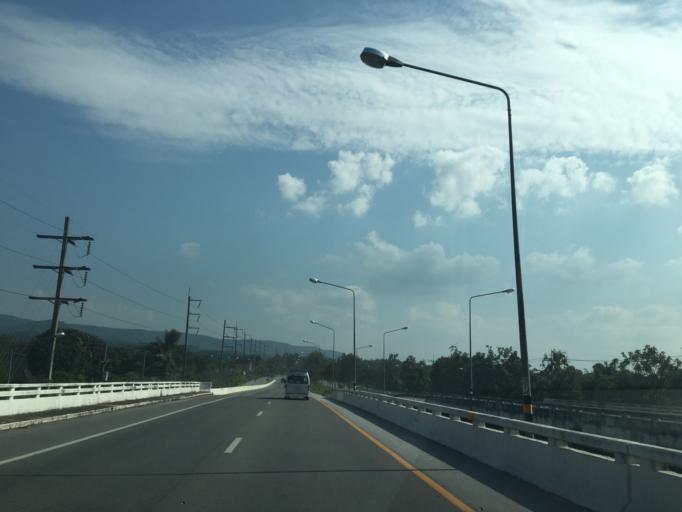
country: TH
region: Chiang Rai
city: Mae Lao
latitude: 19.7145
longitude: 99.7181
